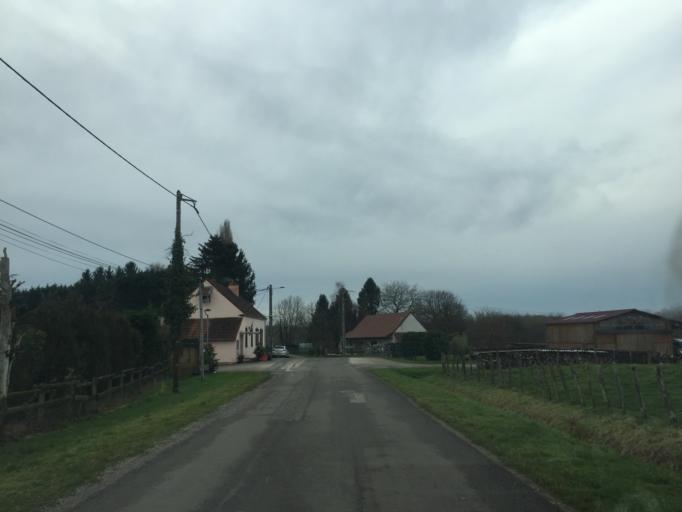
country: FR
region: Franche-Comte
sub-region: Departement du Jura
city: Chaussin
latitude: 46.9027
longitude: 5.4539
